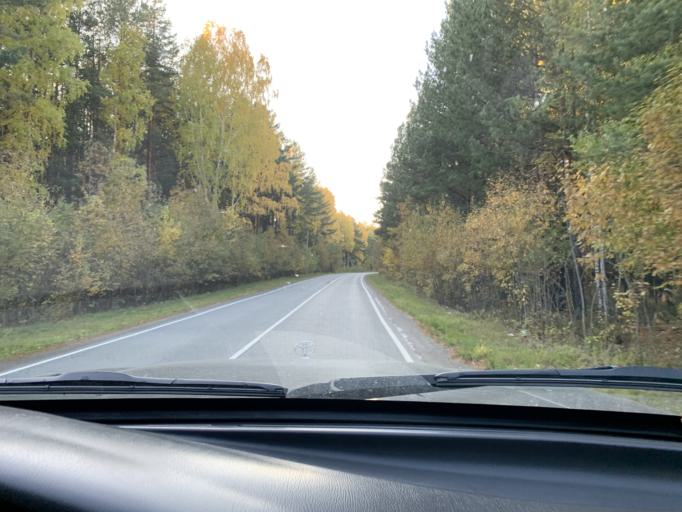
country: RU
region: Sverdlovsk
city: Verkhneye Dubrovo
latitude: 56.8652
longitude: 61.0862
